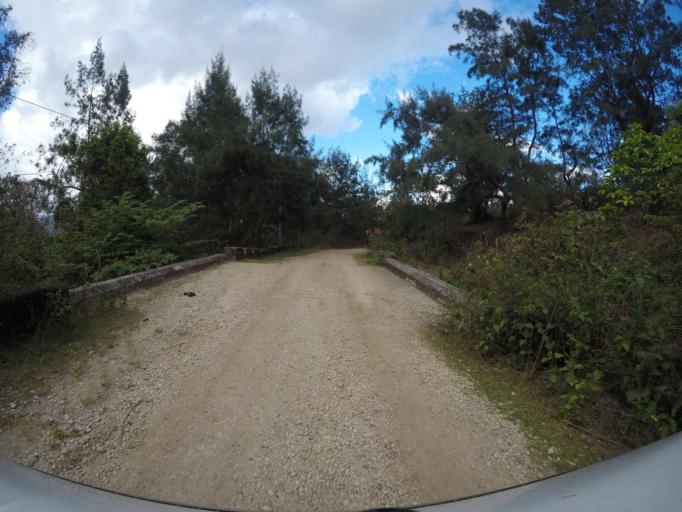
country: TL
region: Baucau
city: Venilale
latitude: -8.6869
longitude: 126.6583
